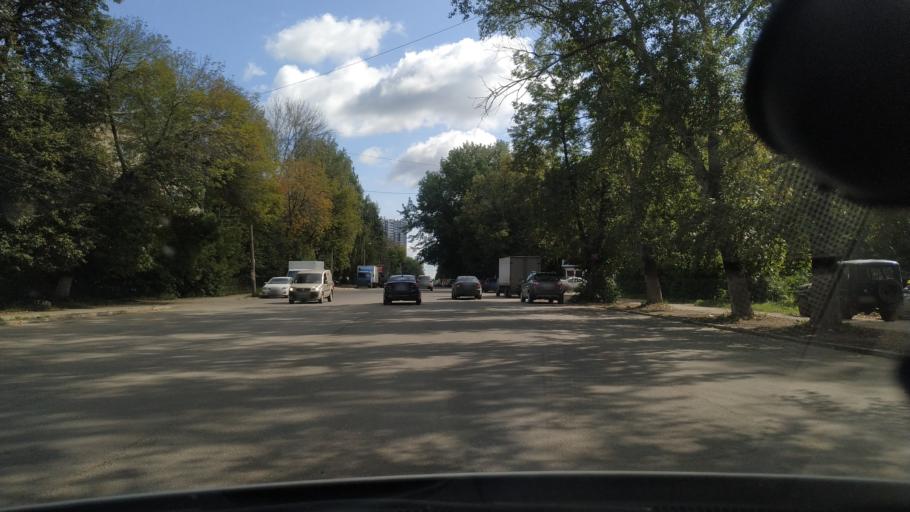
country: RU
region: Rjazan
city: Ryazan'
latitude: 54.6058
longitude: 39.7081
